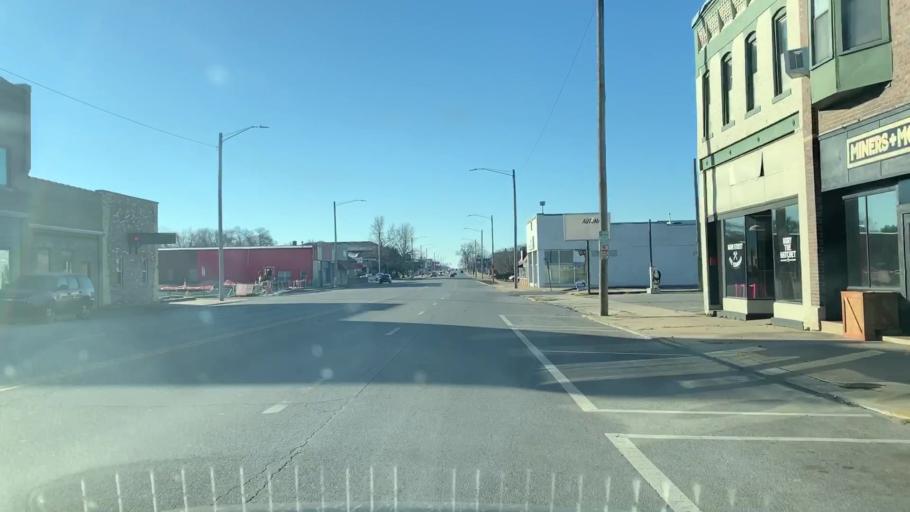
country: US
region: Kansas
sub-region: Crawford County
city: Pittsburg
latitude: 37.4069
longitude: -94.7050
